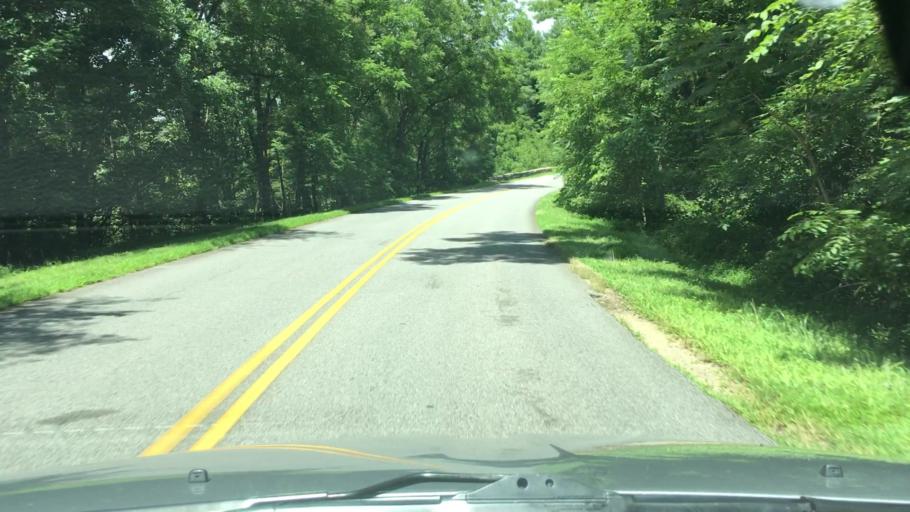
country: US
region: North Carolina
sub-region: Buncombe County
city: Biltmore Forest
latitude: 35.5856
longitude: -82.4789
